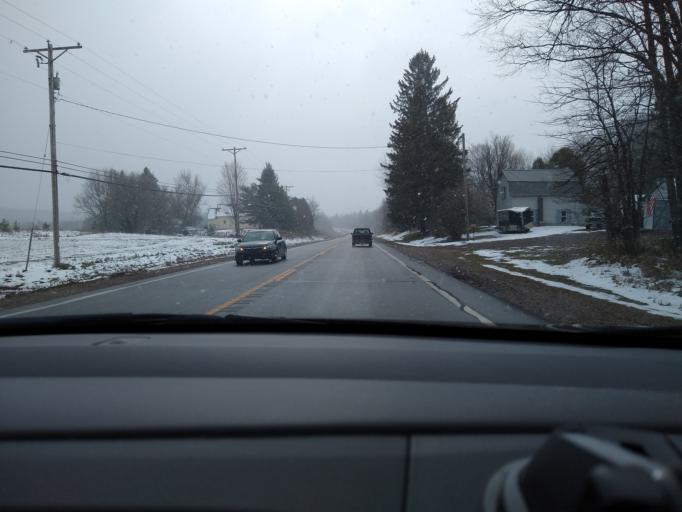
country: US
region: Wisconsin
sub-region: Florence County
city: Florence
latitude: 46.0766
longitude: -88.0752
